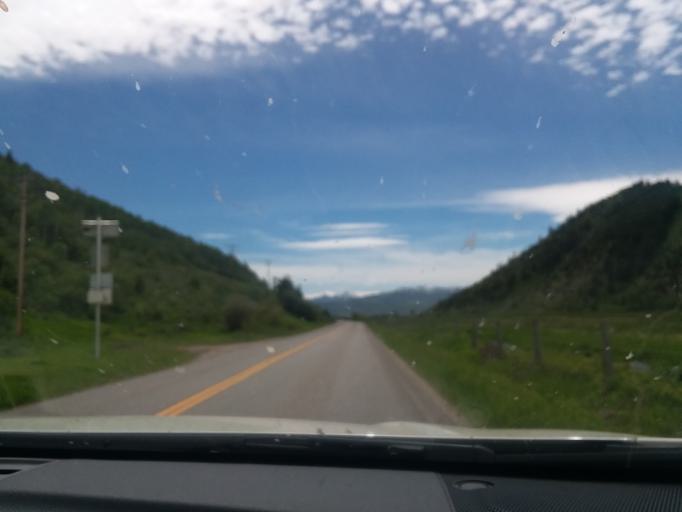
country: US
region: Wyoming
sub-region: Teton County
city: Jackson
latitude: 43.4888
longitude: -110.7904
